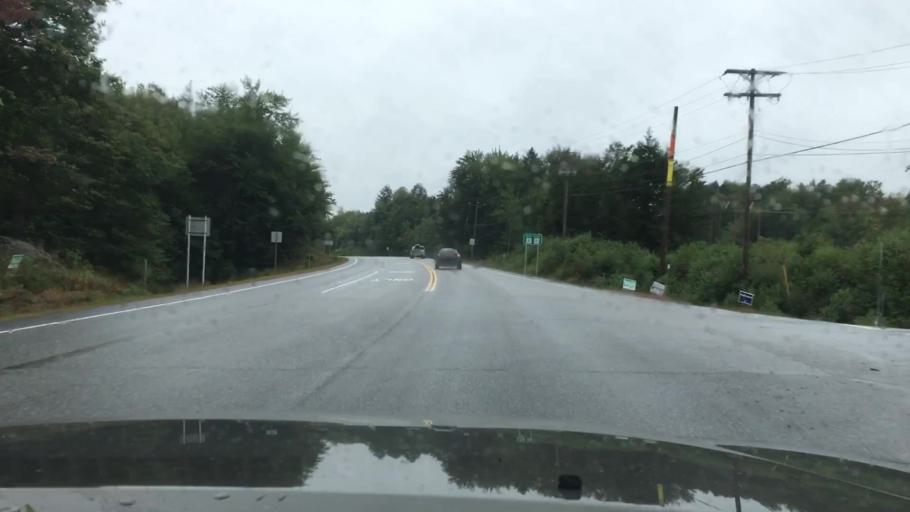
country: US
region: New Hampshire
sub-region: Cheshire County
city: Harrisville
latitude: 43.0570
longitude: -72.0776
